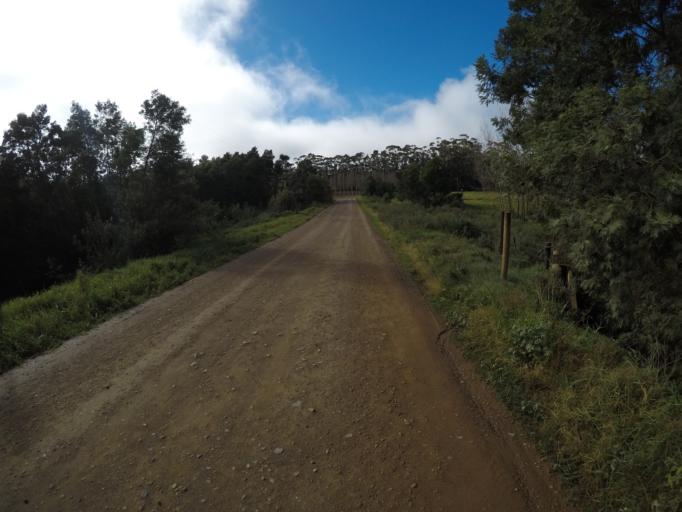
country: ZA
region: Western Cape
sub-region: Cape Winelands District Municipality
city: Ashton
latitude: -34.1118
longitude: 19.7957
